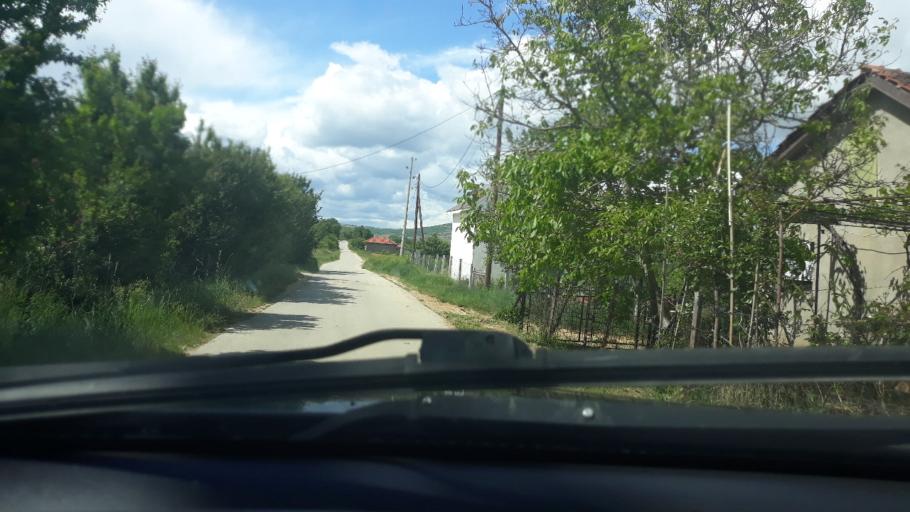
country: MK
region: Krivogastani
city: Krivogashtani
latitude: 41.3489
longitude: 21.2985
